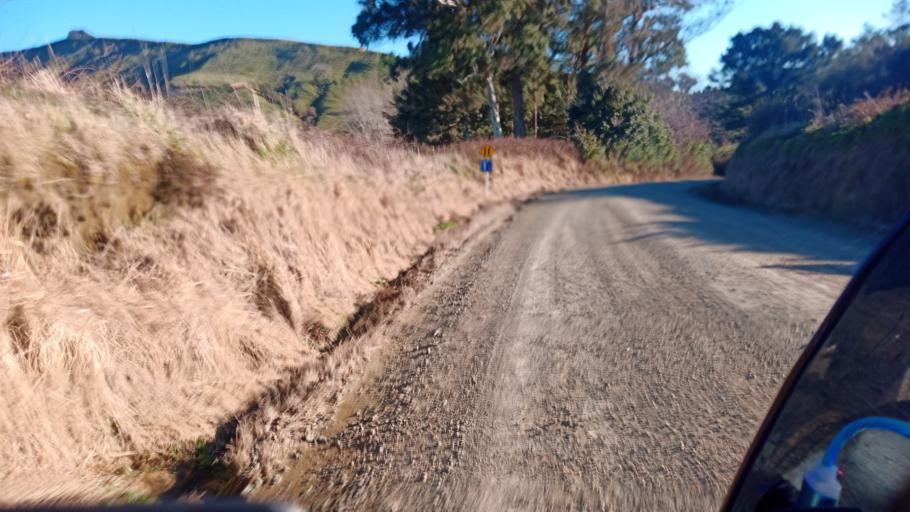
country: NZ
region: Bay of Plenty
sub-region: Opotiki District
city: Opotiki
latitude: -38.4604
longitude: 177.4248
